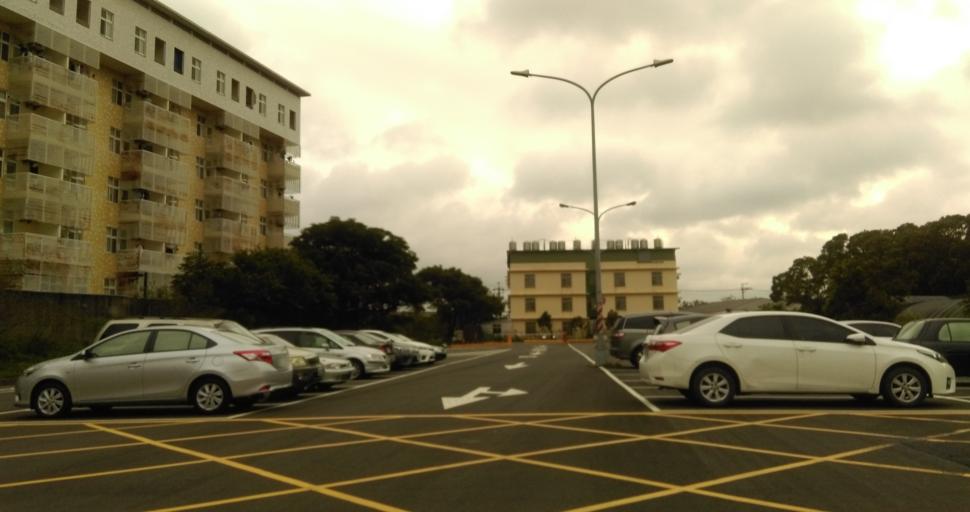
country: TW
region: Taiwan
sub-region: Hsinchu
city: Hsinchu
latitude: 24.7592
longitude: 120.9505
